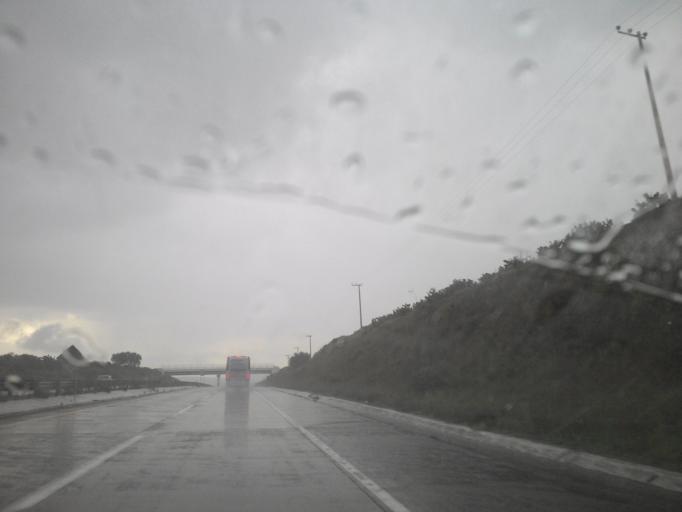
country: MX
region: Hidalgo
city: Zempoala
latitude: 19.8861
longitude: -98.6453
